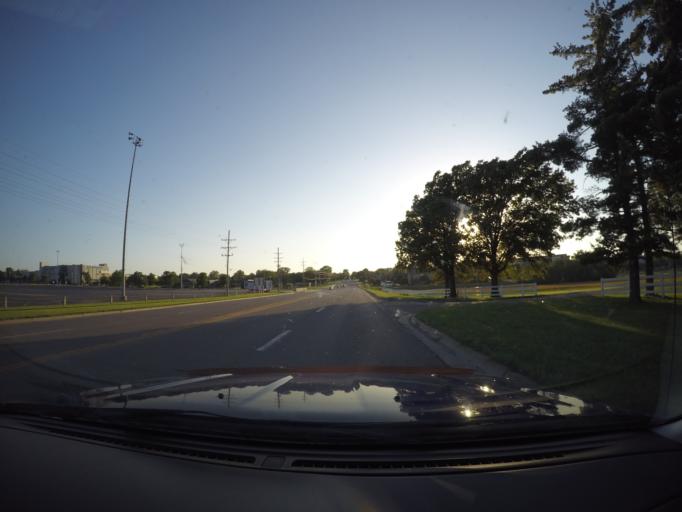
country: US
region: Kansas
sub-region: Riley County
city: Manhattan
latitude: 39.2040
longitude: -96.5962
